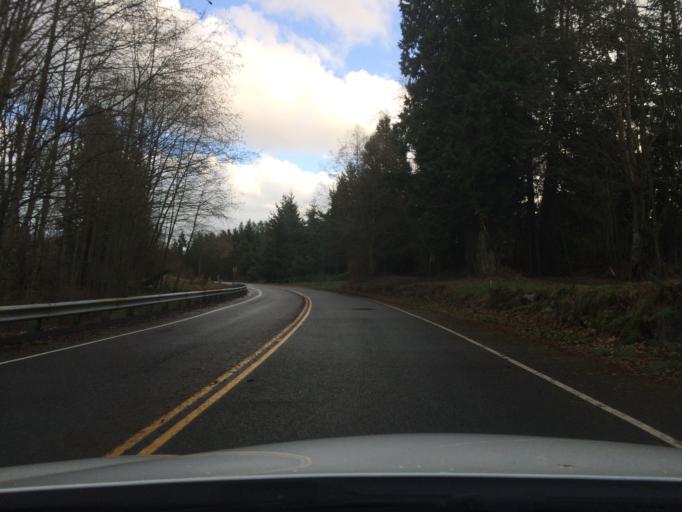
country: US
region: Washington
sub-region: Whatcom County
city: Blaine
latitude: 48.9678
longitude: -122.7849
